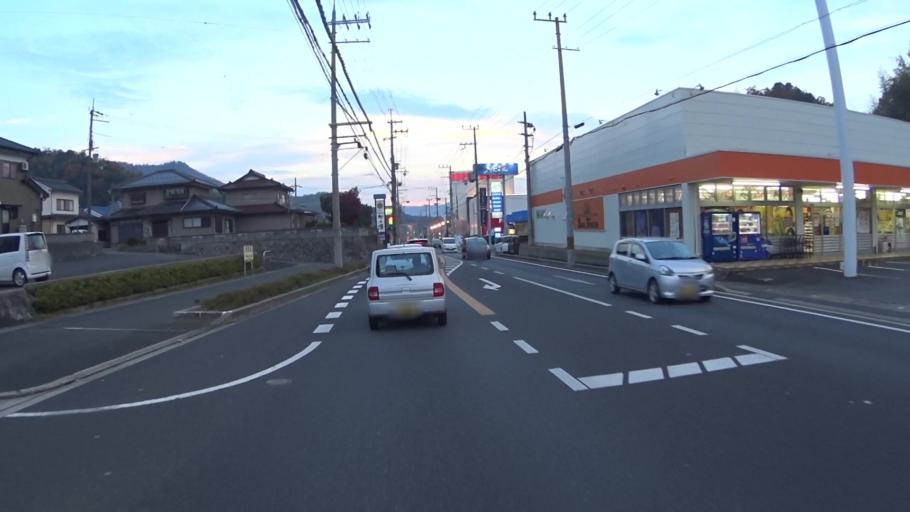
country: JP
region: Kyoto
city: Maizuru
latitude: 35.4501
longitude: 135.3538
